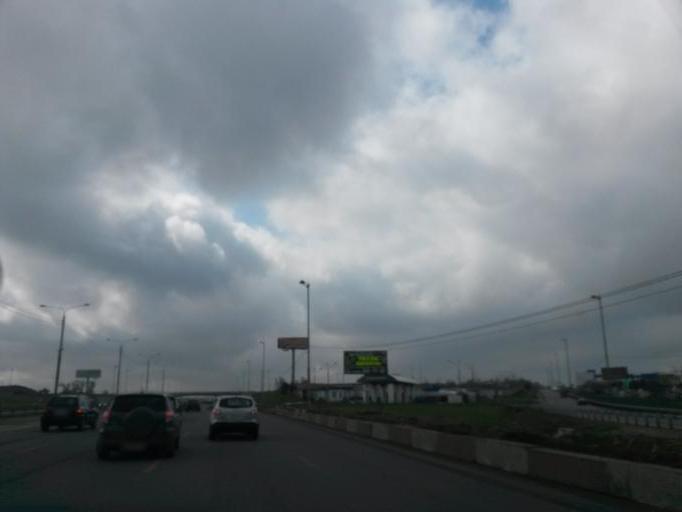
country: RU
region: Moskovskaya
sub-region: Podol'skiy Rayon
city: Podol'sk
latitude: 55.4417
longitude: 37.6157
